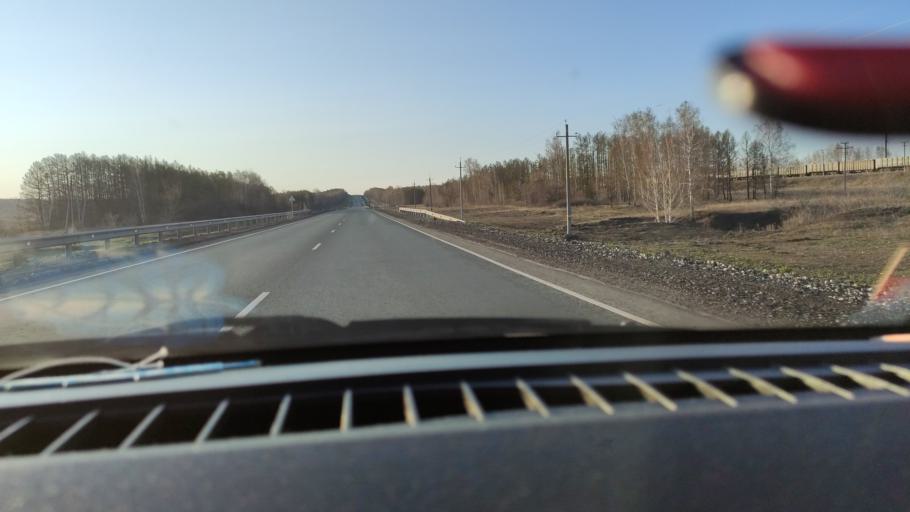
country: RU
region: Saratov
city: Shikhany
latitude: 52.1549
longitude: 47.1804
